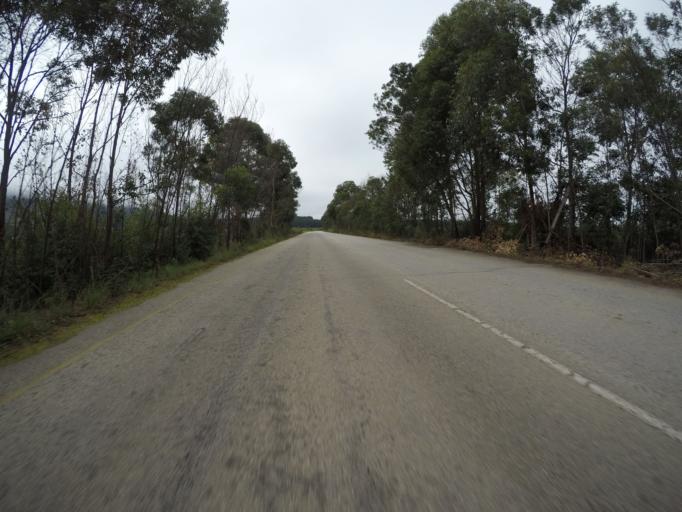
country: ZA
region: Eastern Cape
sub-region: Cacadu District Municipality
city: Kareedouw
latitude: -33.9983
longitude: 24.1718
